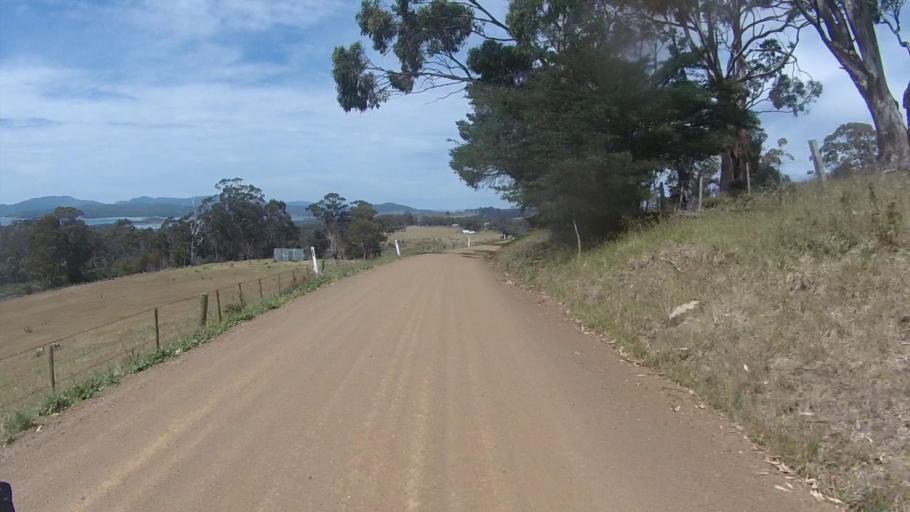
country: AU
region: Tasmania
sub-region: Sorell
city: Sorell
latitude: -42.7946
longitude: 147.8418
